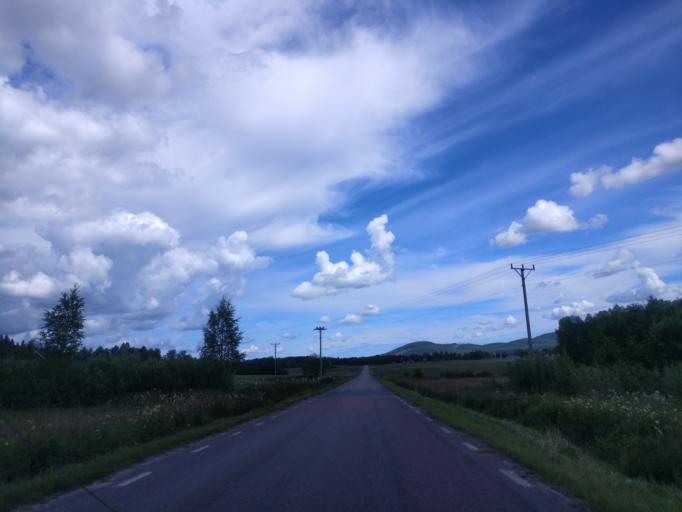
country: SE
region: Vaermland
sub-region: Hagfors Kommun
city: Ekshaerad
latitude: 60.1200
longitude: 13.4520
